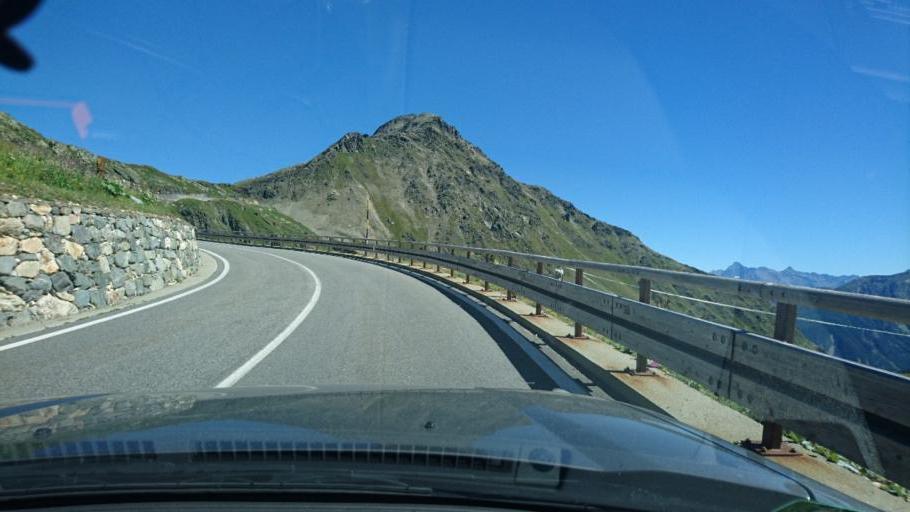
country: IT
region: Aosta Valley
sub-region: Valle d'Aosta
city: San Leonardo
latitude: 45.8677
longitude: 7.1526
